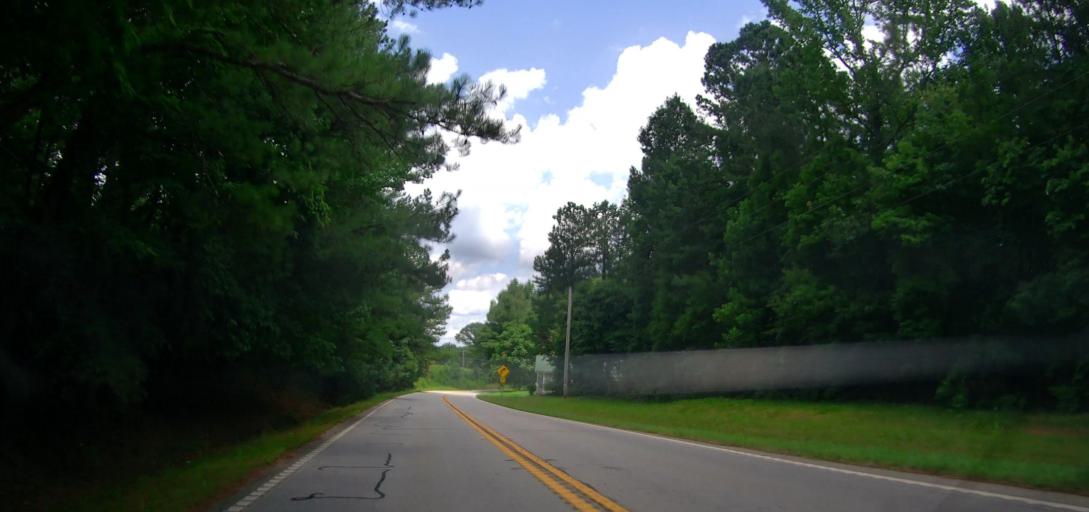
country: US
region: Georgia
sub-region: Heard County
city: Franklin
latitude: 33.3150
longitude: -85.1503
